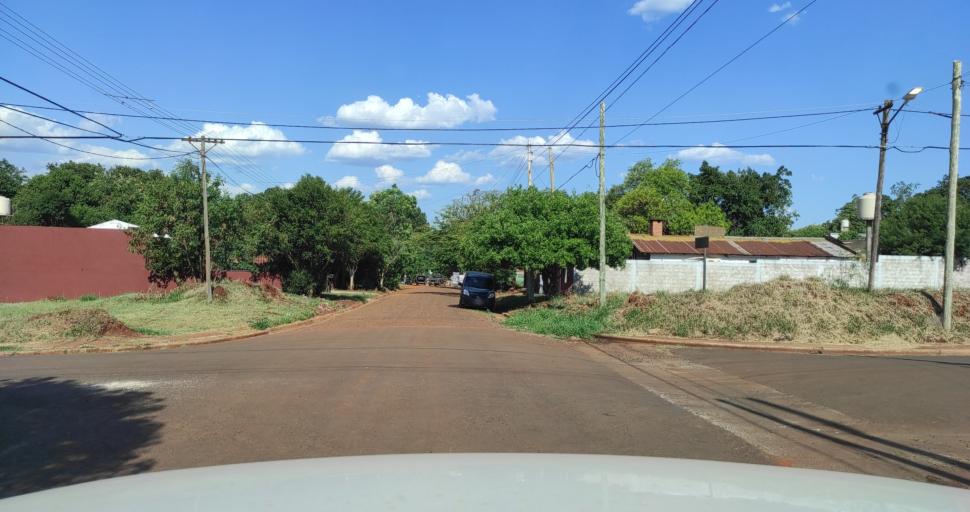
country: AR
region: Misiones
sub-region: Departamento de Capital
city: Posadas
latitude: -27.4156
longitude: -55.9261
